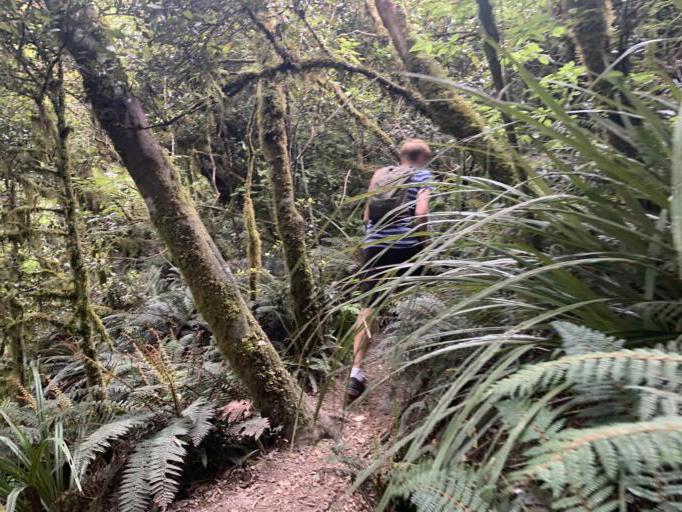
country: NZ
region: Waikato
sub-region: Taupo District
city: Taupo
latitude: -38.6954
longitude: 176.1593
